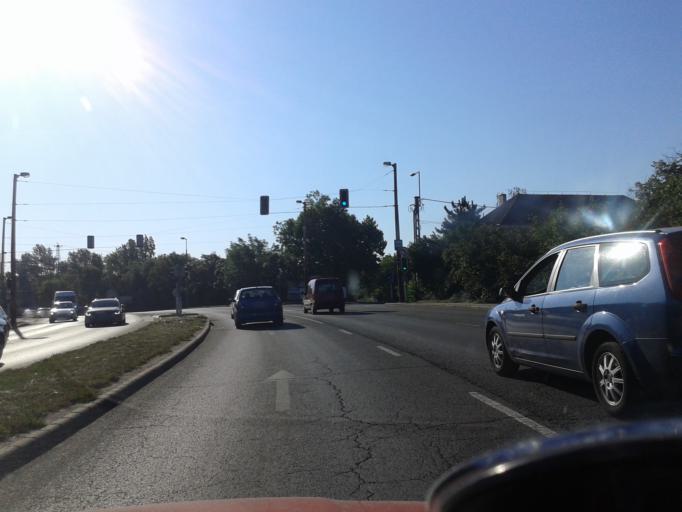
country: HU
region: Budapest
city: Budapest XI. keruelet
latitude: 47.4541
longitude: 19.0212
